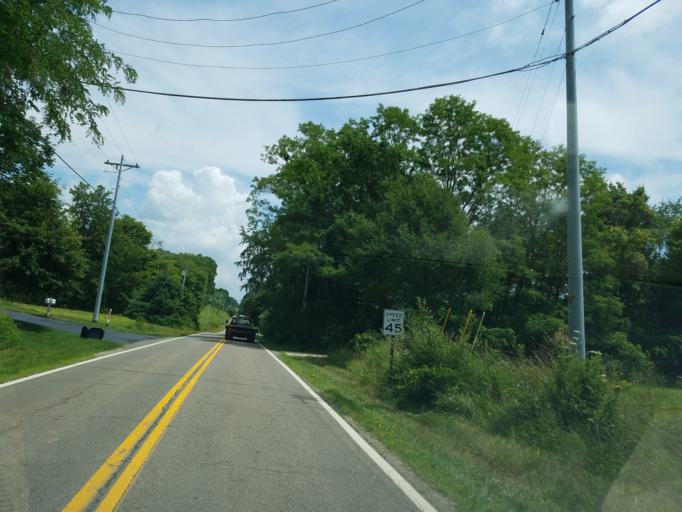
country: US
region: Ohio
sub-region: Licking County
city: Granville
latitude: 40.1538
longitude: -82.5551
